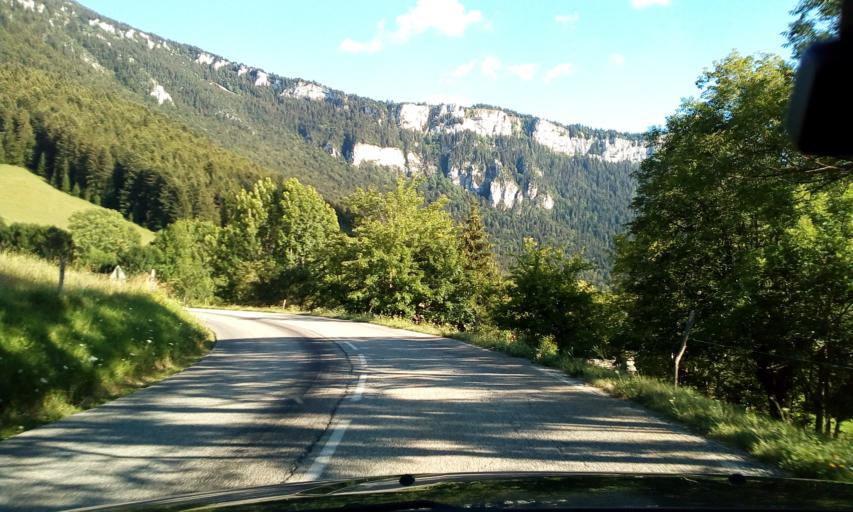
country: FR
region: Rhone-Alpes
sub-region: Departement de l'Isere
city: Lans-en-Vercors
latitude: 45.1559
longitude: 5.6192
